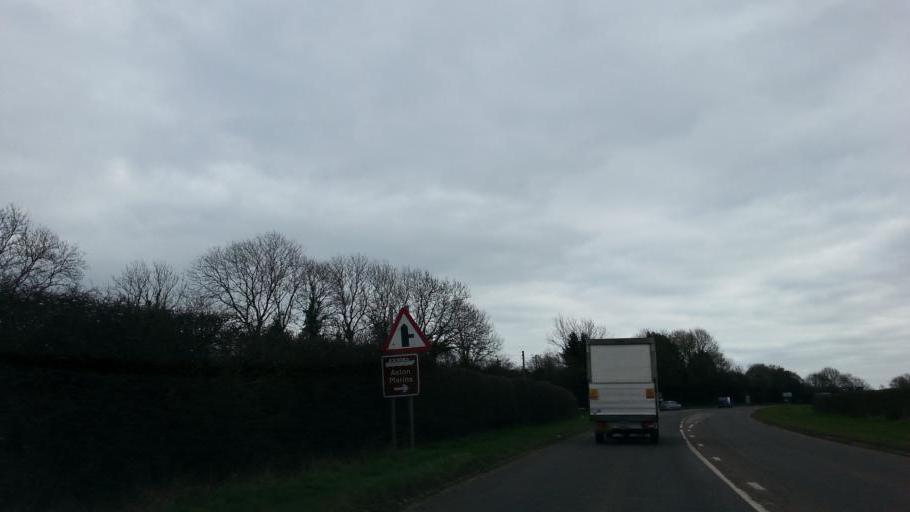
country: GB
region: England
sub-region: Staffordshire
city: Stone
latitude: 52.8874
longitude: -2.1231
